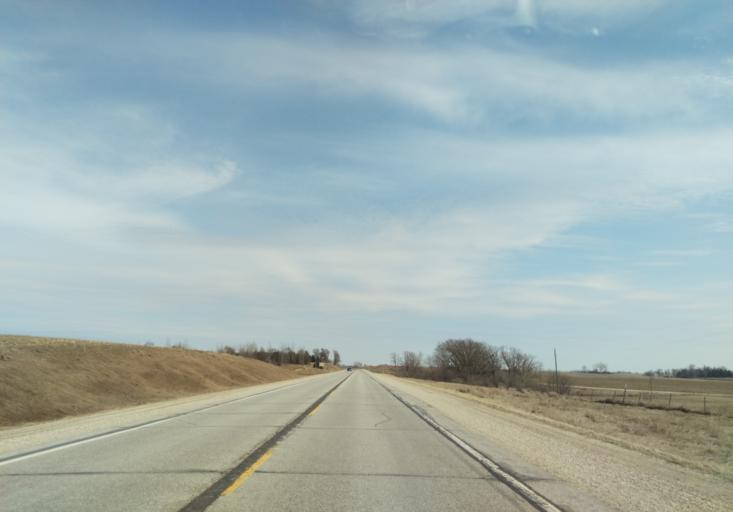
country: US
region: Iowa
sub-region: Allamakee County
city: Waukon
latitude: 43.2407
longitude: -91.5508
